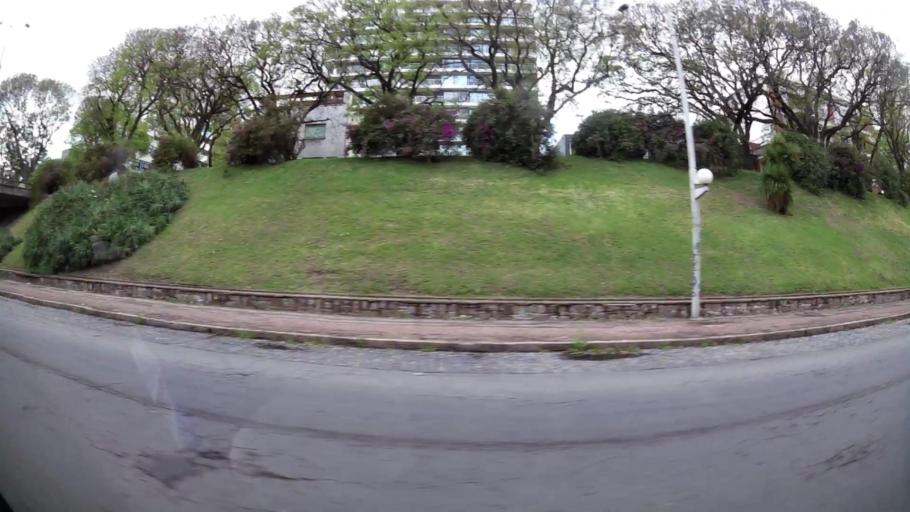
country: UY
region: Montevideo
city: Montevideo
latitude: -34.9150
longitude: -56.1626
